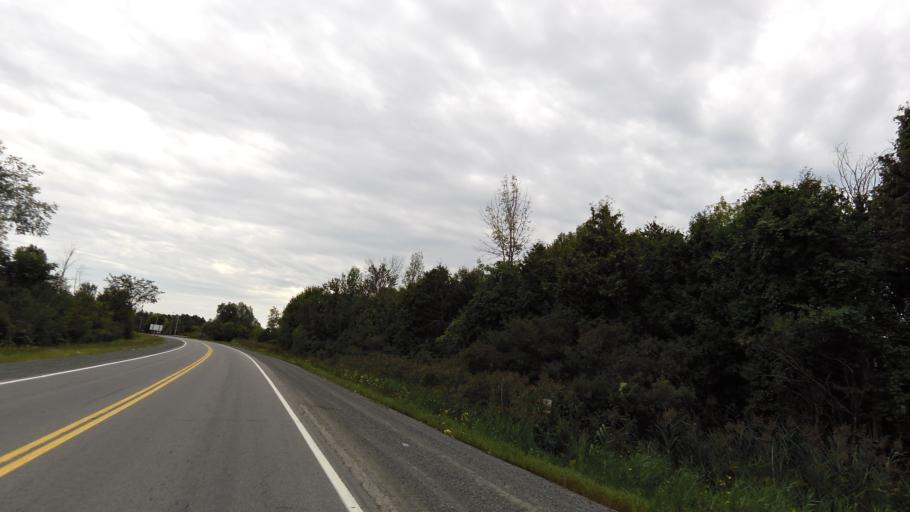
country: CA
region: Ontario
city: Ottawa
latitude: 45.2663
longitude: -75.5624
